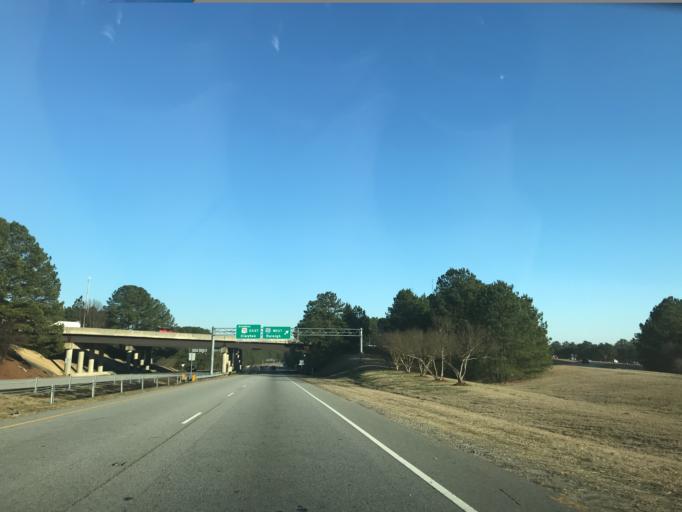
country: US
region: North Carolina
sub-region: Wake County
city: Garner
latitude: 35.6949
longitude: -78.5768
